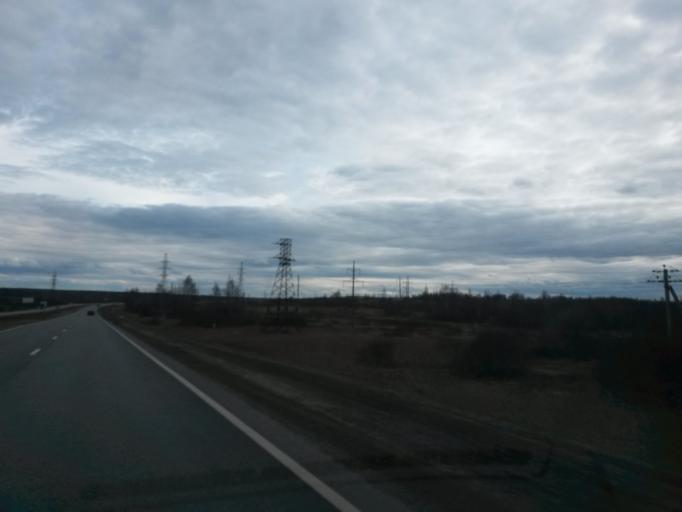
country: RU
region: Jaroslavl
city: Krasnyye Tkachi
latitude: 57.5211
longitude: 39.7852
